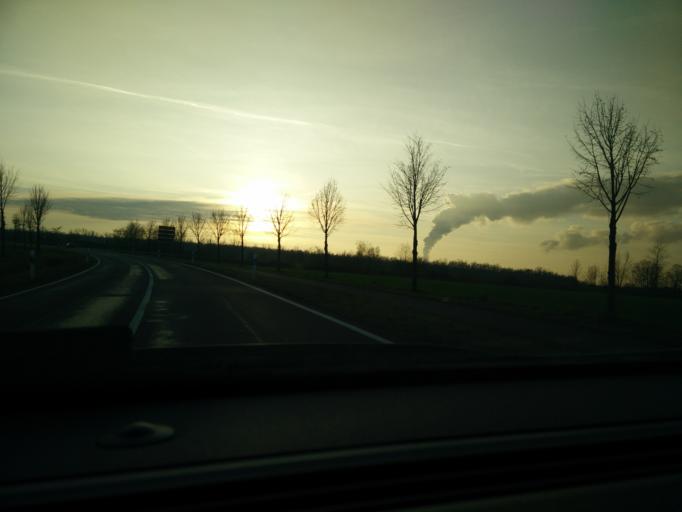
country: DE
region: Saxony
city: Espenhain
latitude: 51.2147
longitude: 12.4506
